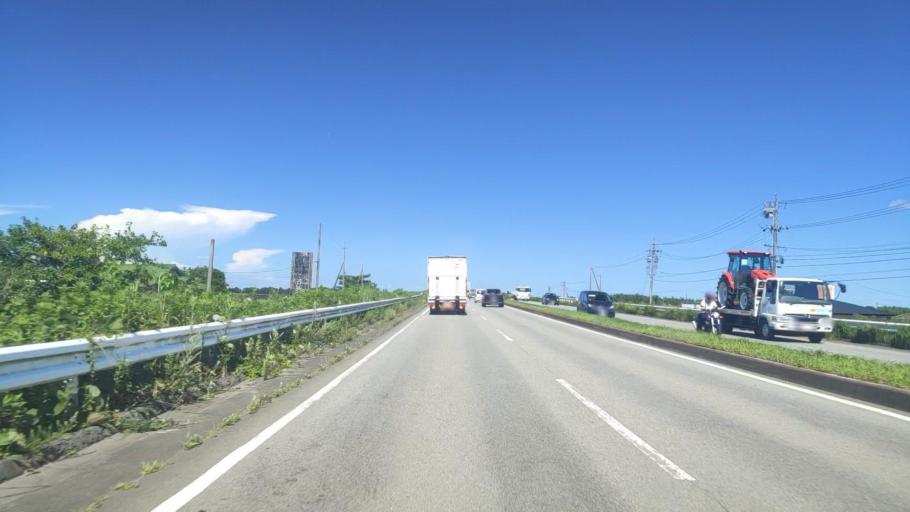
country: JP
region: Mie
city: Hisai-motomachi
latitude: 34.5851
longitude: 136.5797
